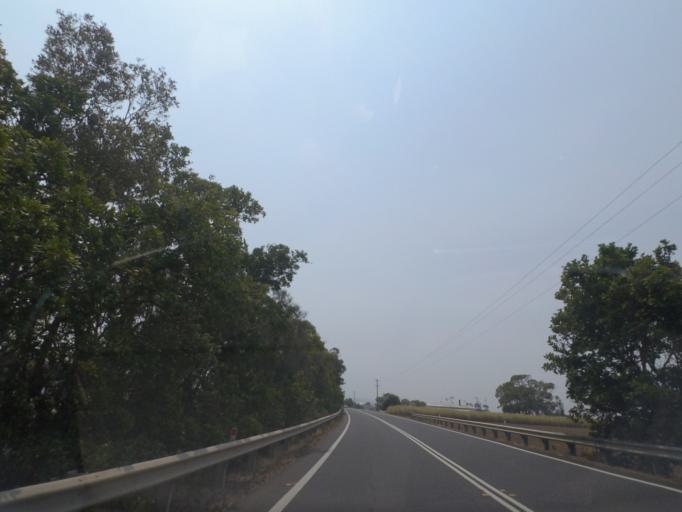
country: AU
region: New South Wales
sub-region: Richmond Valley
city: Evans Head
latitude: -28.9819
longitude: 153.4622
